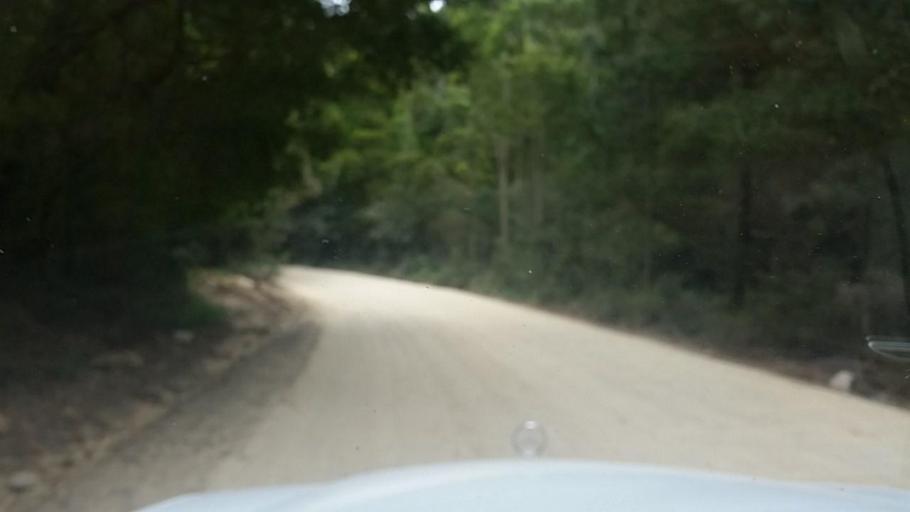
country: ZA
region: Western Cape
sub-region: Eden District Municipality
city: Knysna
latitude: -33.9747
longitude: 23.1440
